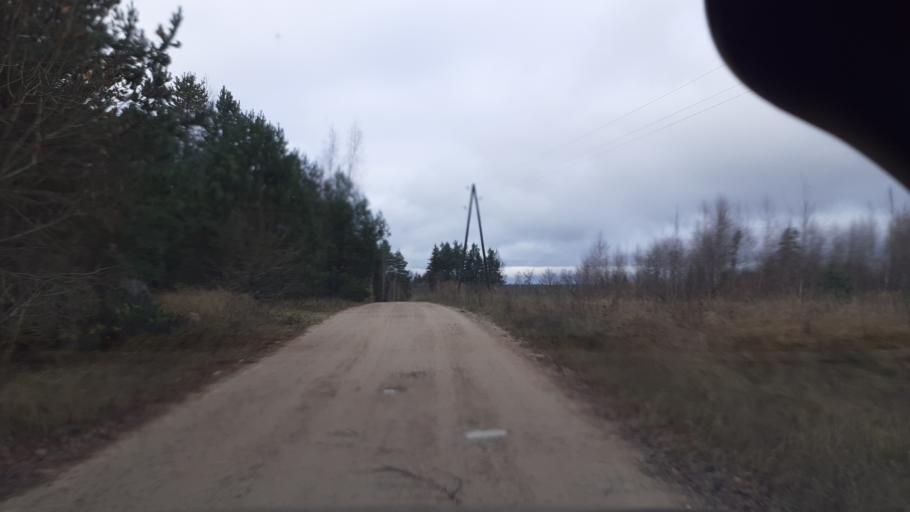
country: LV
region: Kuldigas Rajons
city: Kuldiga
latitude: 57.0382
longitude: 21.8802
